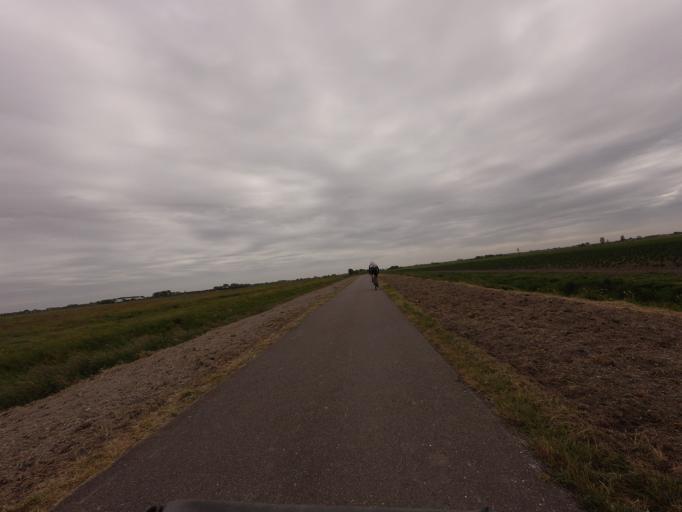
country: NL
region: North Holland
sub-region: Gemeente Medemblik
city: Opperdoes
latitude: 52.7355
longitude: 5.0567
